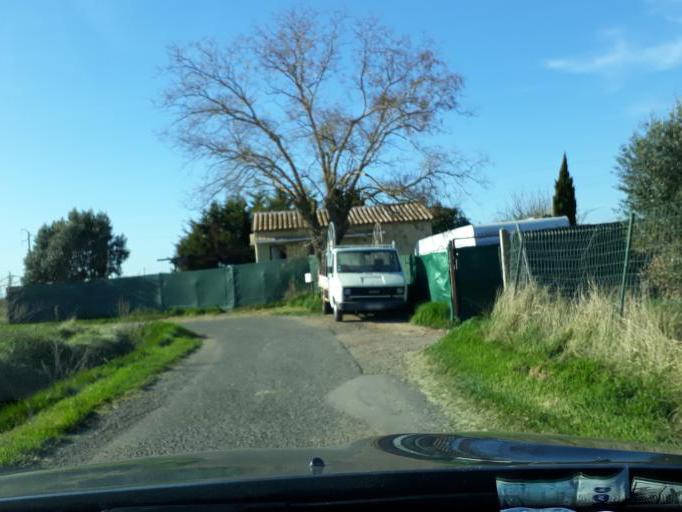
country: FR
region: Languedoc-Roussillon
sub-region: Departement de l'Herault
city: Agde
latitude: 43.3218
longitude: 3.4584
